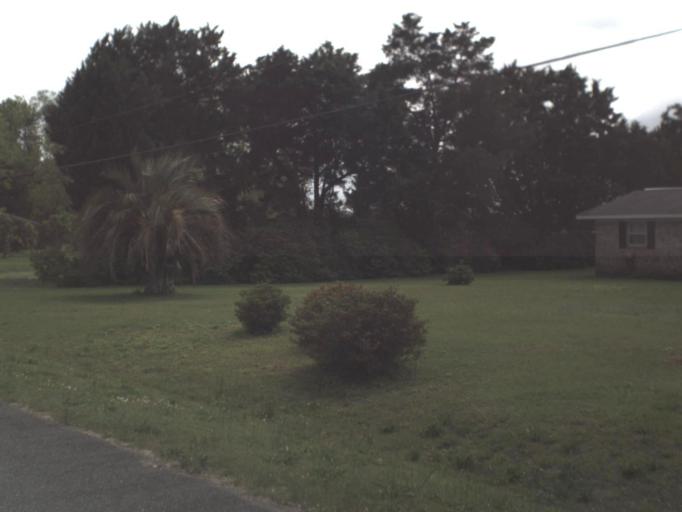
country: US
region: Florida
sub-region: Santa Rosa County
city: Point Baker
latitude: 30.7066
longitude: -87.0785
